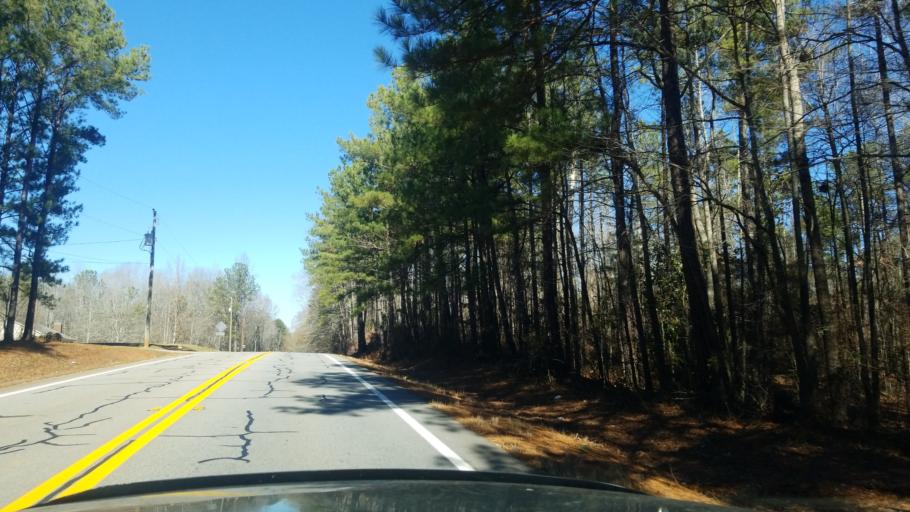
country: US
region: Georgia
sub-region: Harris County
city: Hamilton
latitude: 32.6648
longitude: -84.8585
